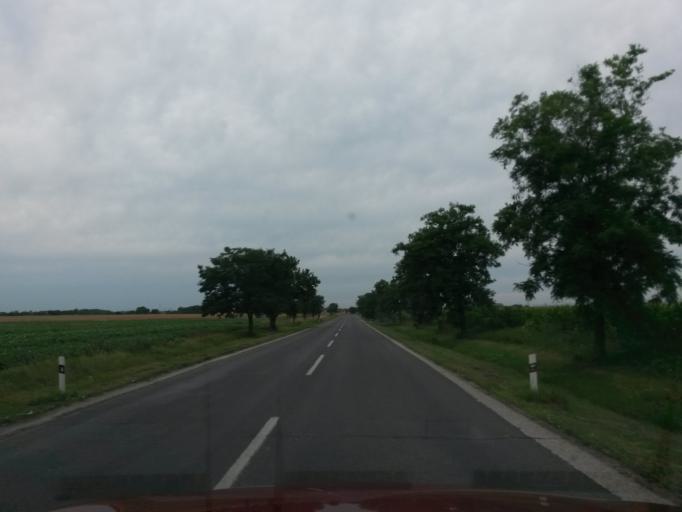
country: SK
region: Nitriansky
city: Surany
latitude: 48.0900
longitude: 18.2721
